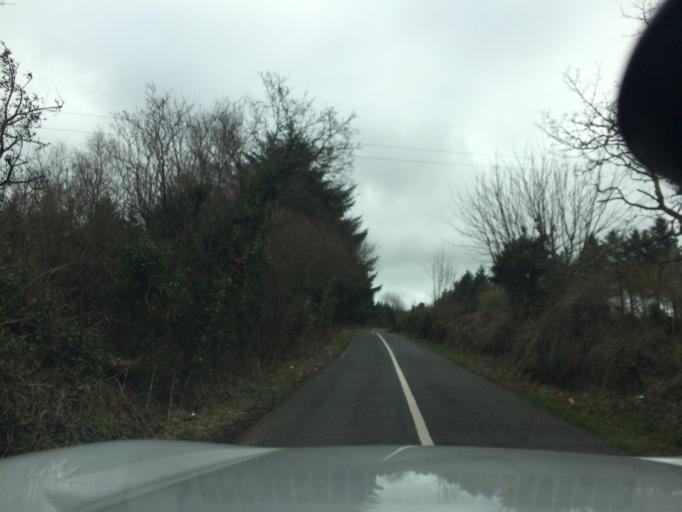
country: IE
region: Munster
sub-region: South Tipperary
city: Cluain Meala
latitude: 52.3370
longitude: -7.6229
